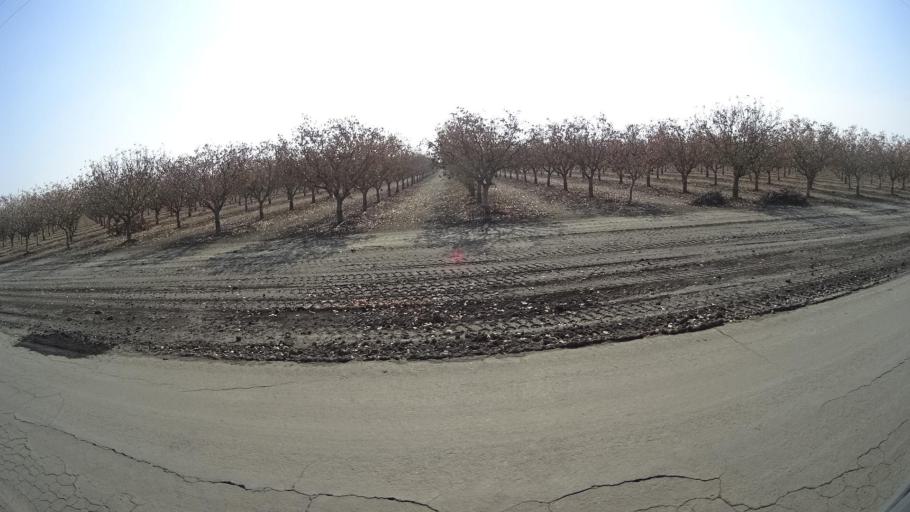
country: US
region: California
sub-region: Kern County
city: Buttonwillow
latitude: 35.3693
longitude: -119.4409
